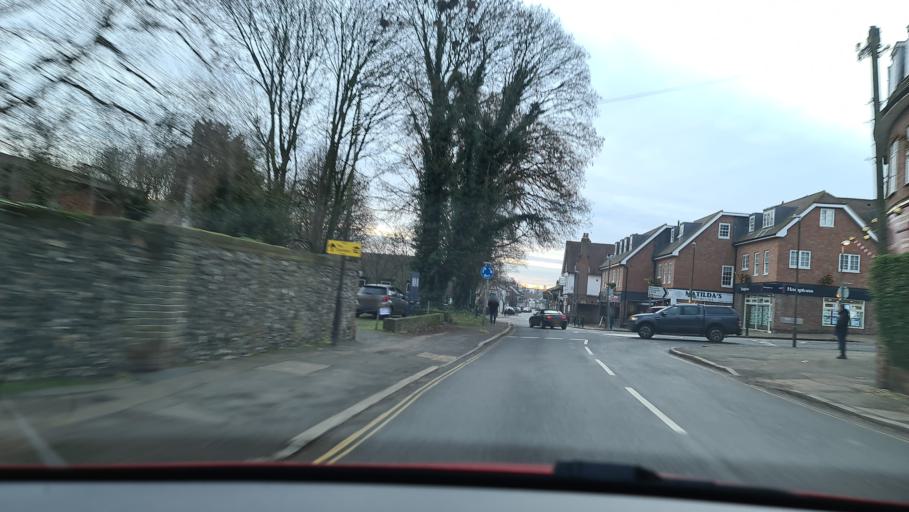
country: GB
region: England
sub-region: Buckinghamshire
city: Great Missenden
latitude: 51.7047
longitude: -0.7082
